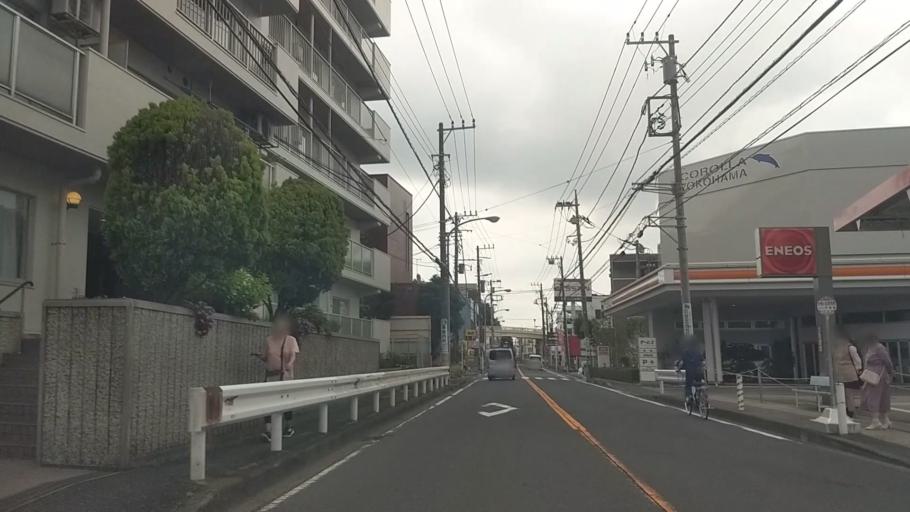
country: JP
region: Kanagawa
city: Kamakura
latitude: 35.3856
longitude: 139.5362
